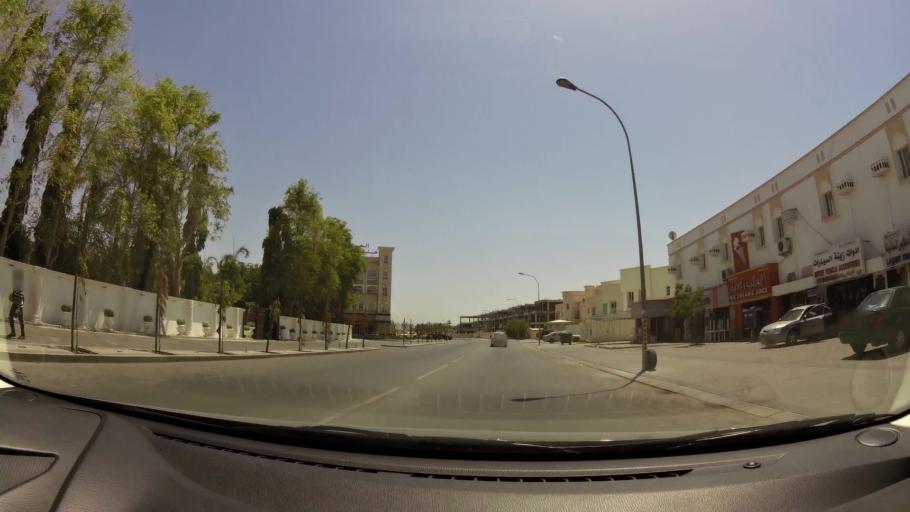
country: OM
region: Muhafazat Masqat
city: As Sib al Jadidah
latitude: 23.6322
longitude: 58.2285
